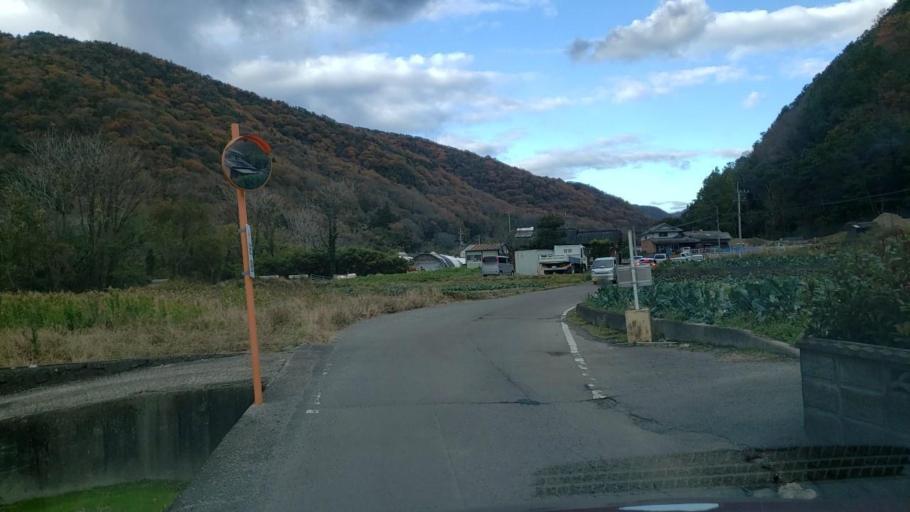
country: JP
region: Tokushima
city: Wakimachi
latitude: 34.1065
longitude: 134.2241
